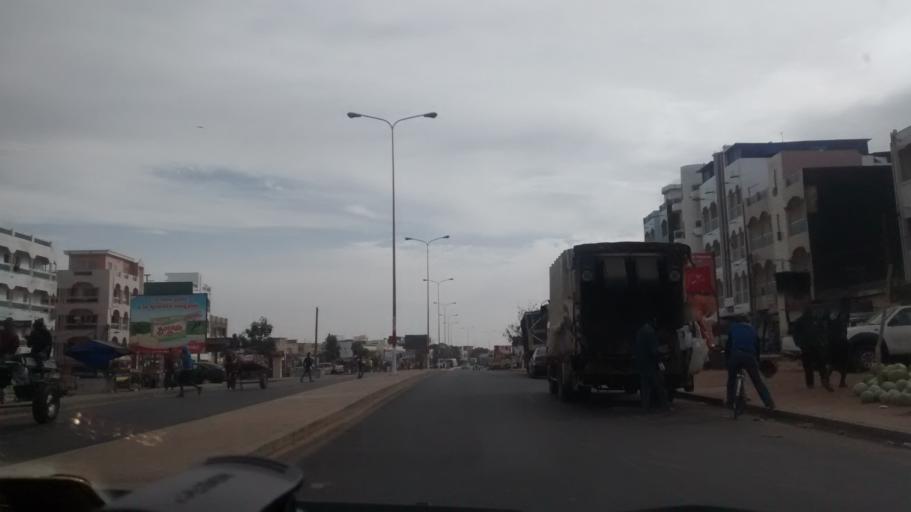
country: SN
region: Dakar
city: Pikine
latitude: 14.7764
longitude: -17.3978
